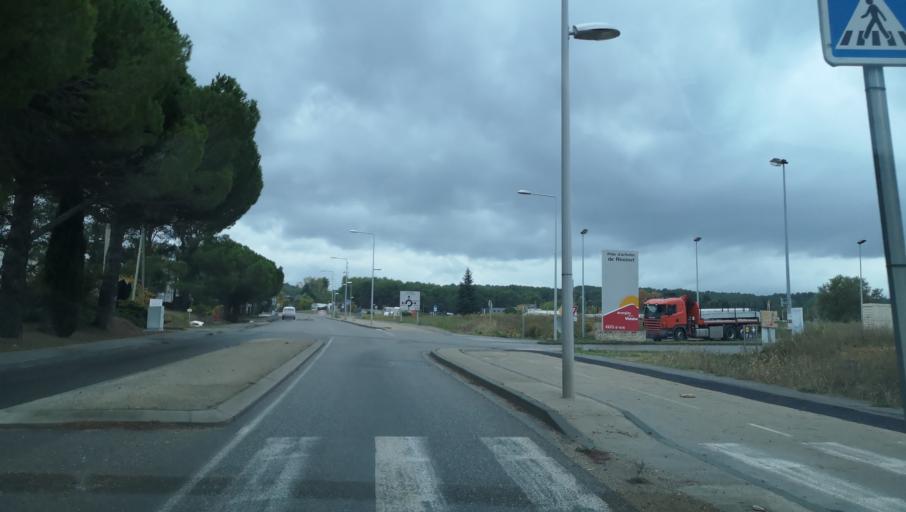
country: FR
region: Provence-Alpes-Cote d'Azur
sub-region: Departement des Bouches-du-Rhone
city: Rousset
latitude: 43.4656
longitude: 5.6119
